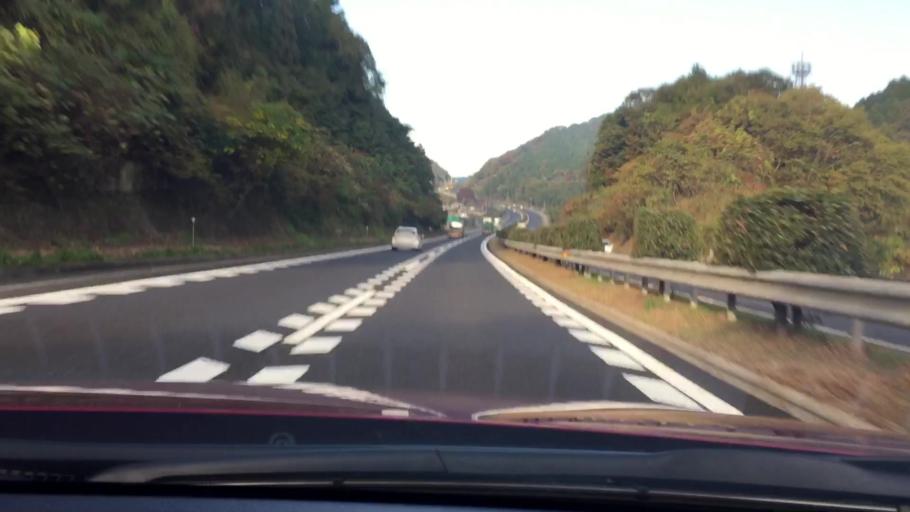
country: JP
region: Hyogo
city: Yamazakicho-nakabirose
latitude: 34.9764
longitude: 134.6381
